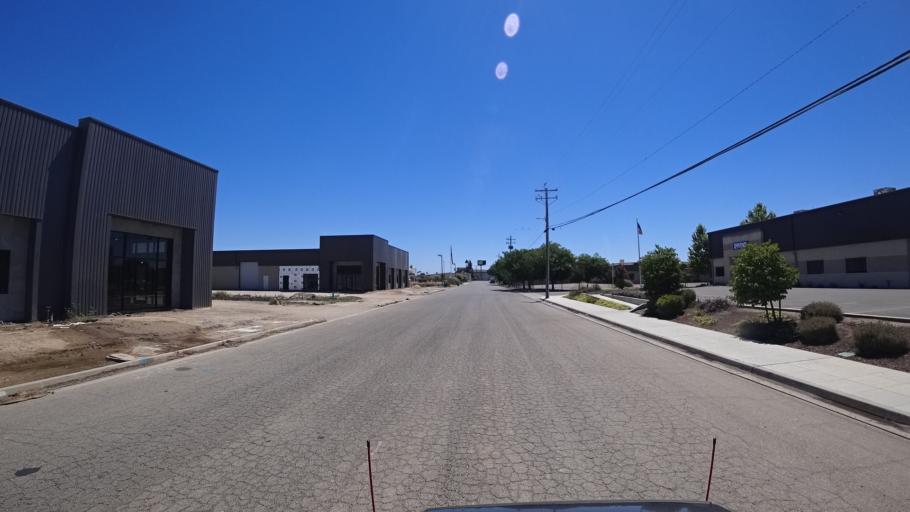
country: US
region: California
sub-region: Fresno County
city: Fresno
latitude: 36.7042
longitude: -119.7767
